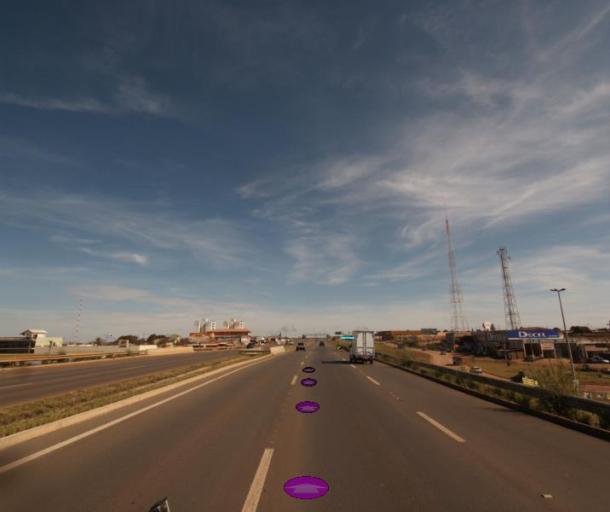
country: BR
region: Federal District
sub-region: Brasilia
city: Brasilia
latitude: -15.7554
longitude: -48.2565
